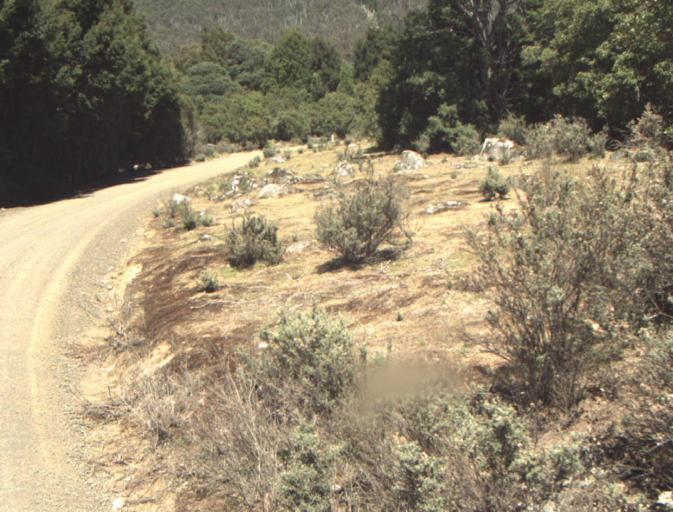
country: AU
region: Tasmania
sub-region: Dorset
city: Scottsdale
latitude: -41.3627
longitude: 147.4305
